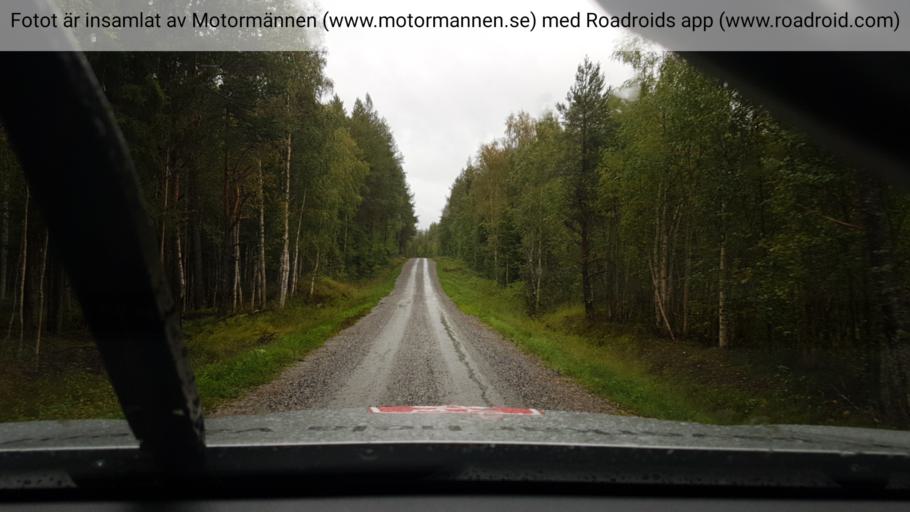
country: SE
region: Vaesterbotten
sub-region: Asele Kommun
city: Asele
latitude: 63.9802
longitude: 17.5752
